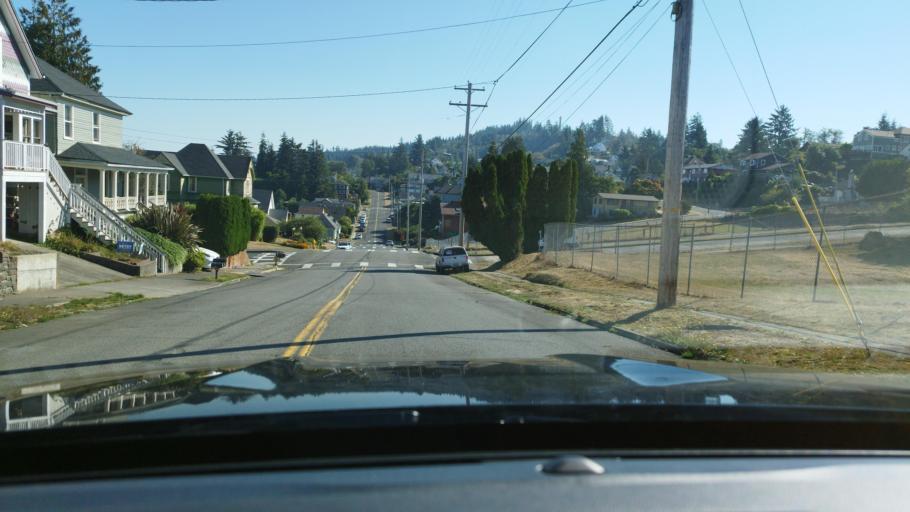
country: US
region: Oregon
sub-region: Clatsop County
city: Astoria
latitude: 46.1849
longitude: -123.8346
